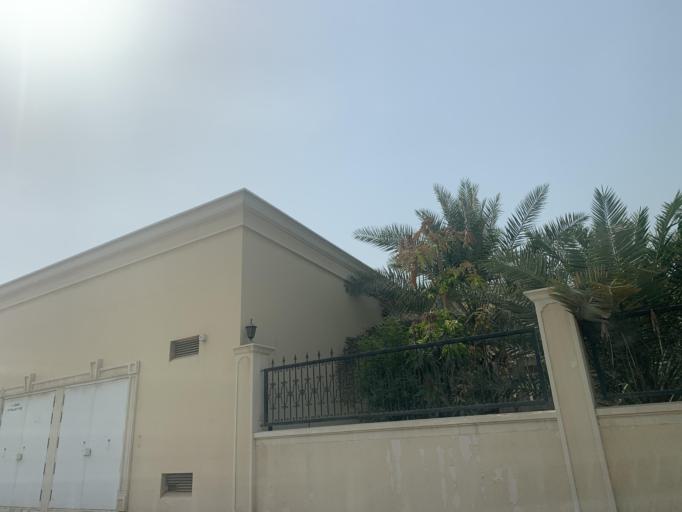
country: BH
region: Manama
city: Jidd Hafs
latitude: 26.2017
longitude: 50.4810
